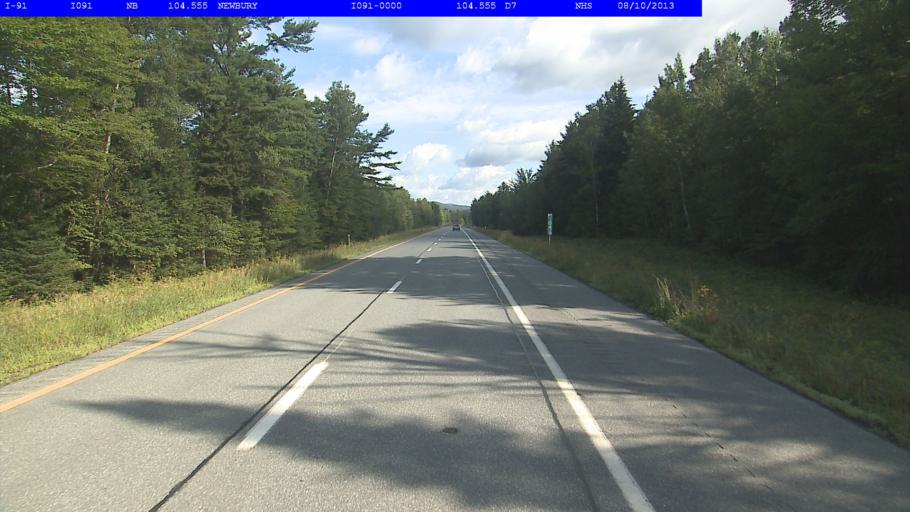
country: US
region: New Hampshire
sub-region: Grafton County
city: Haverhill
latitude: 44.0790
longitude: -72.1116
